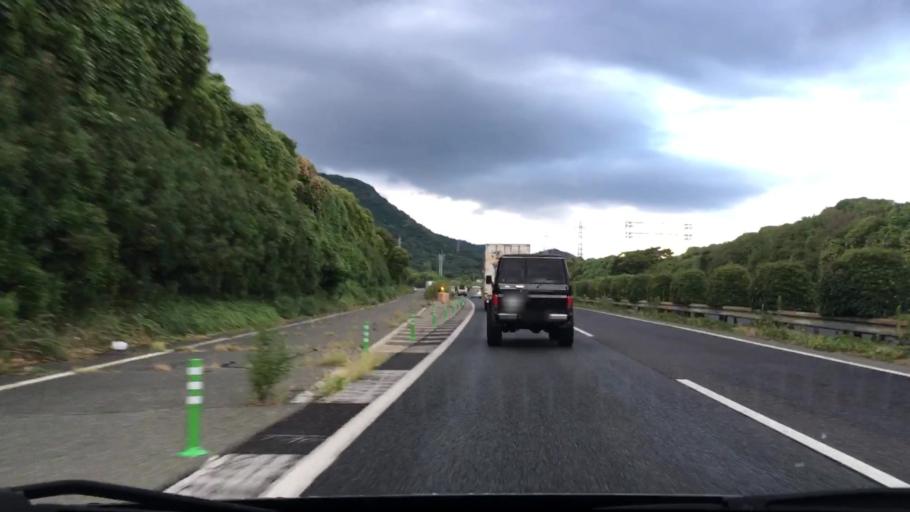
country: JP
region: Fukuoka
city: Kanda
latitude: 33.8418
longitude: 130.9277
